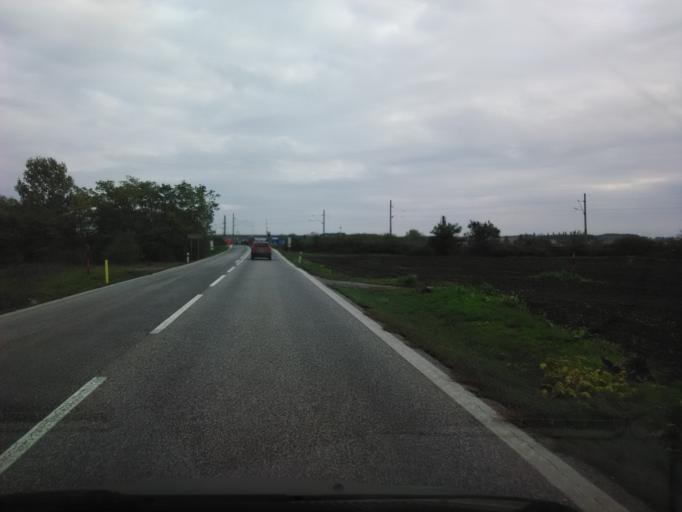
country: SK
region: Nitriansky
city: Tlmace
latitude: 48.2058
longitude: 18.5039
